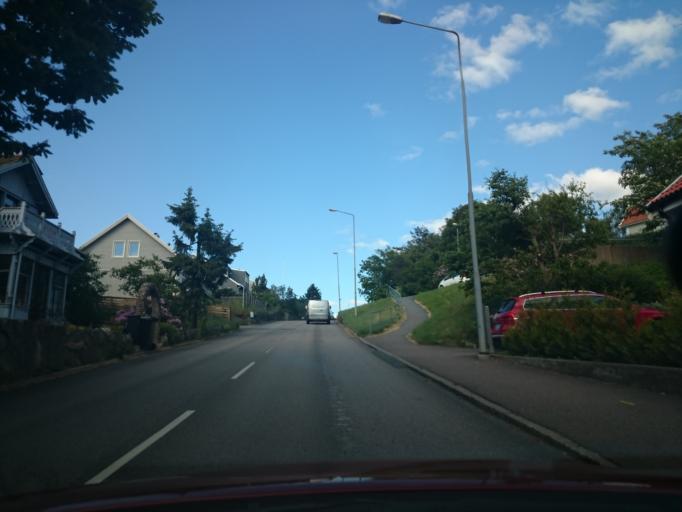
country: SE
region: Vaestra Goetaland
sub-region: Molndal
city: Moelndal
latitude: 57.6641
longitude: 12.0291
